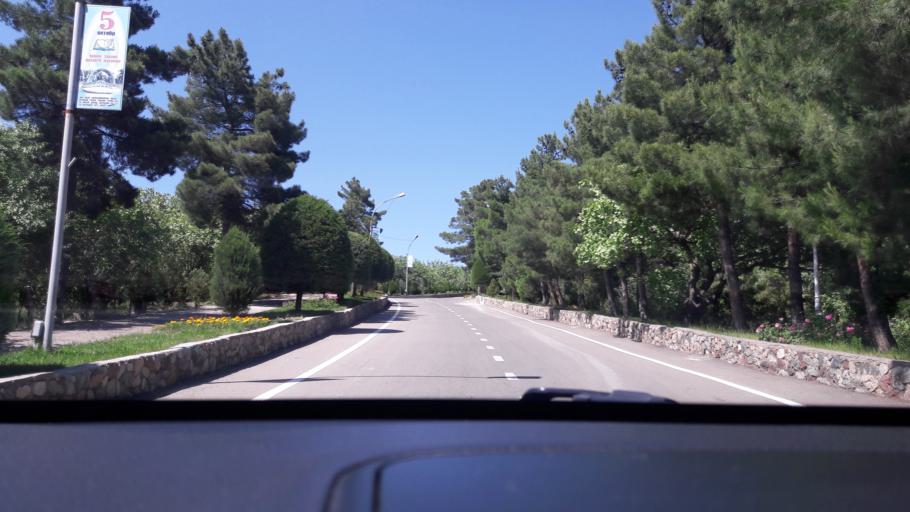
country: TJ
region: Dushanbe
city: Dushanbe
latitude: 38.5796
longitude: 68.8110
